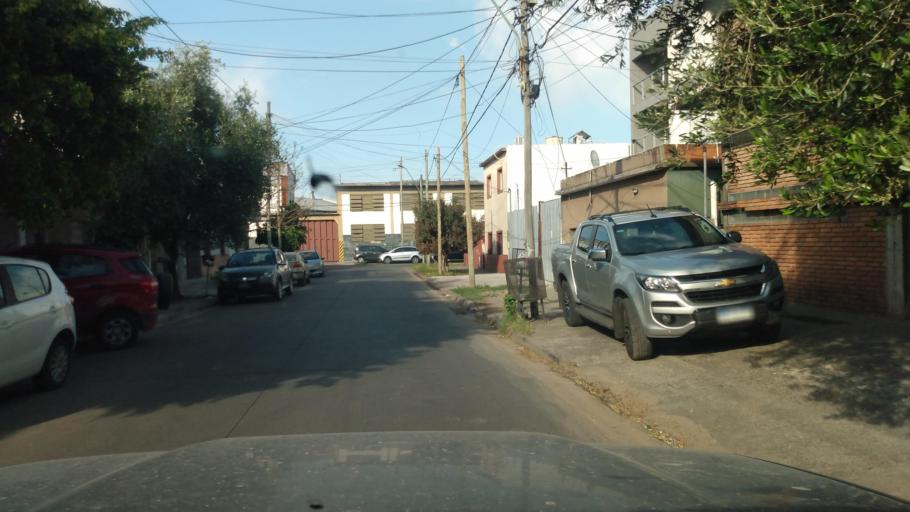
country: AR
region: Buenos Aires
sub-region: Partido de Moron
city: Moron
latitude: -34.6352
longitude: -58.6201
